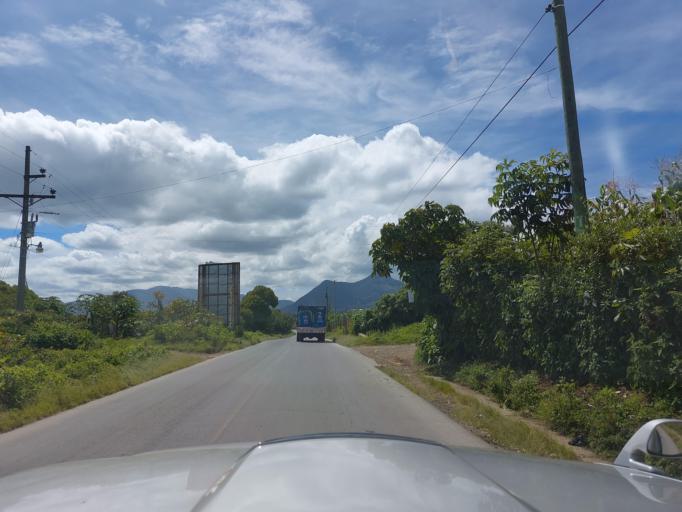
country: GT
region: Chimaltenango
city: San Andres Itzapa
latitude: 14.6179
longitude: -90.8303
